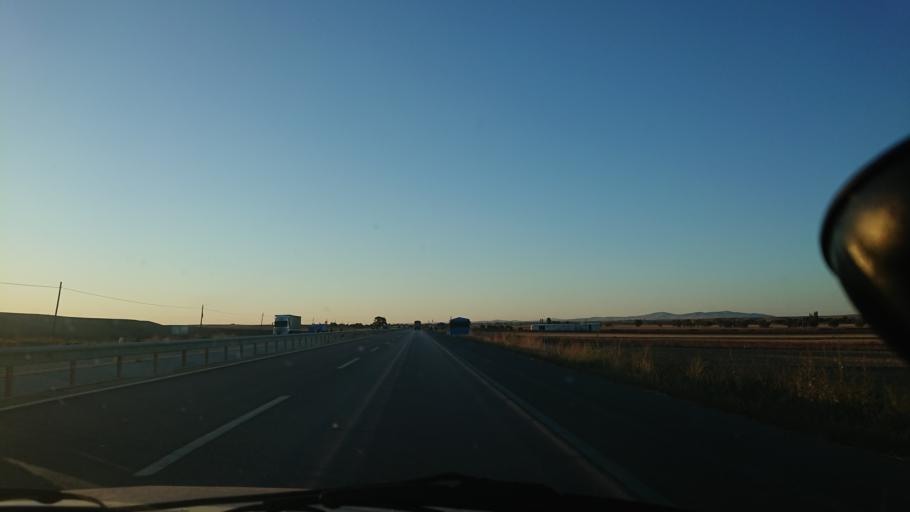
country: TR
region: Eskisehir
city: Mahmudiye
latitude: 39.5232
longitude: 30.9573
